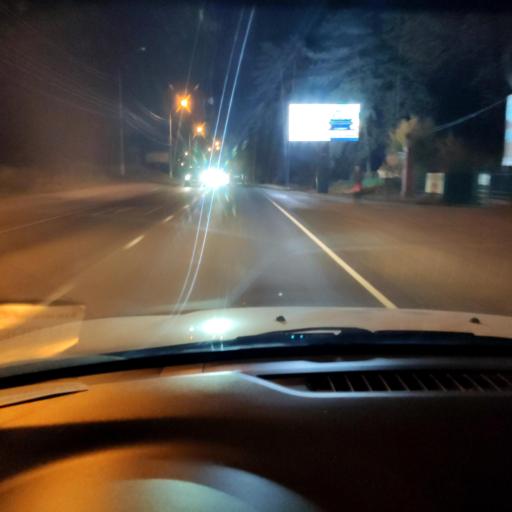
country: RU
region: Samara
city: Tol'yatti
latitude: 53.4846
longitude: 49.3160
